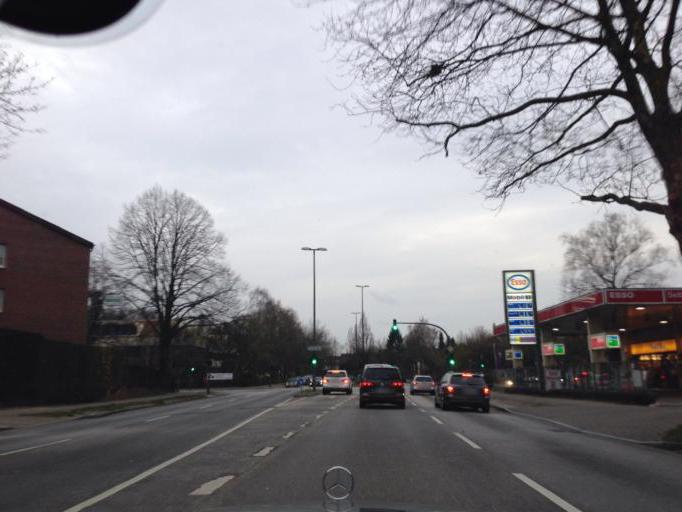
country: DE
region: Hamburg
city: Farmsen-Berne
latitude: 53.6249
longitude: 10.1457
